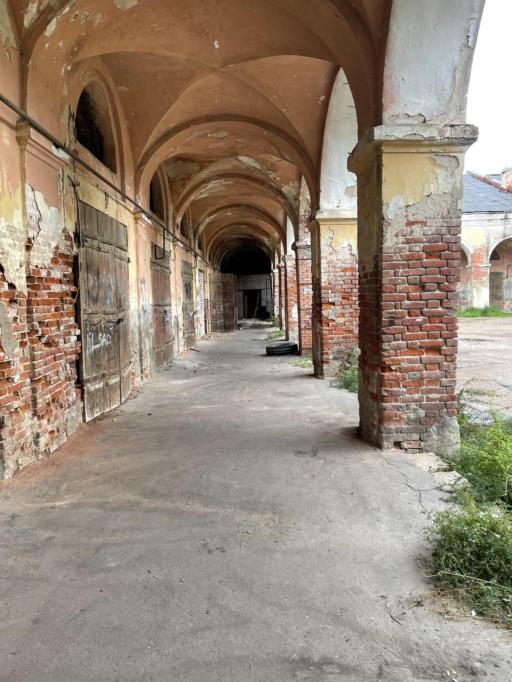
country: RU
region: Tverskaya
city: Vyshniy Volochek
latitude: 57.5833
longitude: 34.5588
